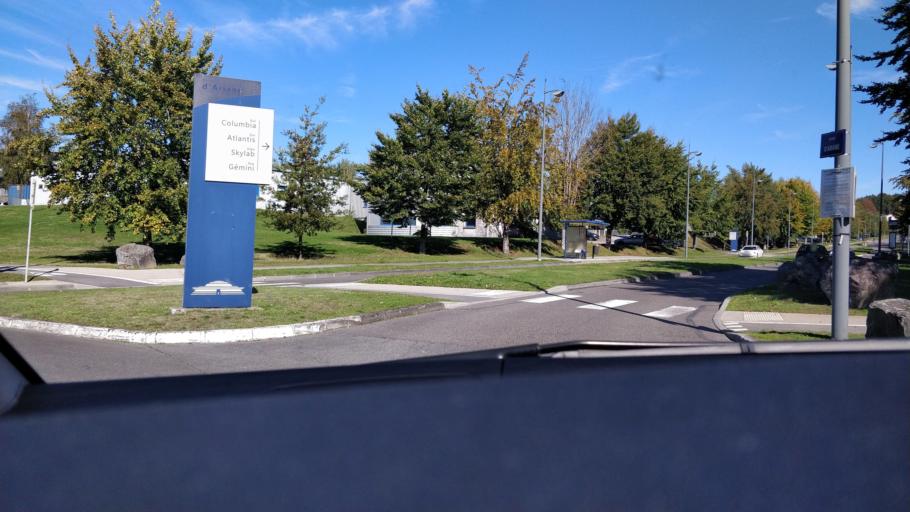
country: FR
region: Limousin
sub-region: Departement de la Haute-Vienne
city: Le Palais-sur-Vienne
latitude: 45.8612
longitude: 1.2910
